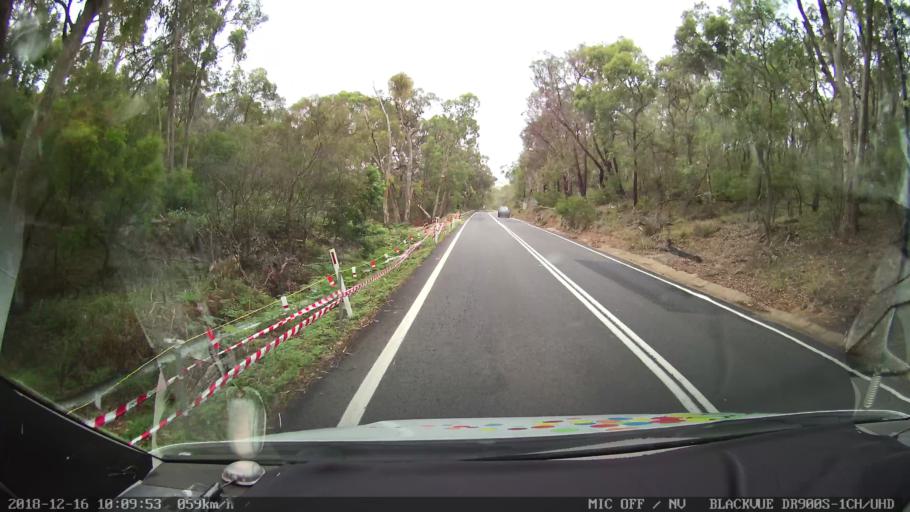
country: AU
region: New South Wales
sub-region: Glen Innes Severn
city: Glen Innes
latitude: -29.3215
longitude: 151.9193
